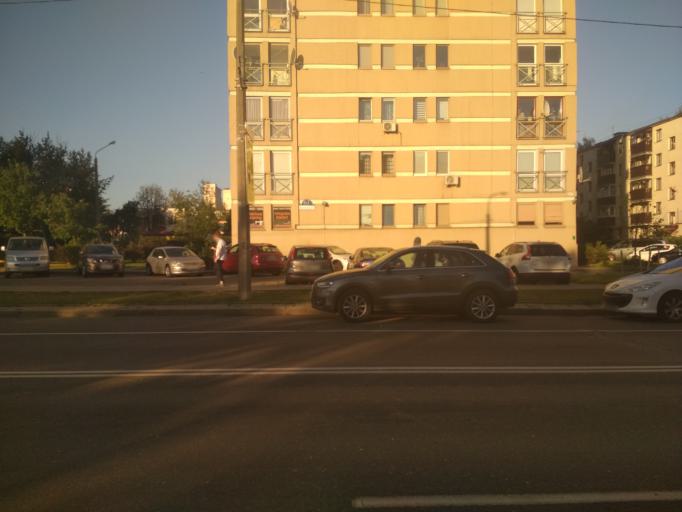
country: BY
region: Minsk
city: Minsk
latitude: 53.8982
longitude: 27.5869
